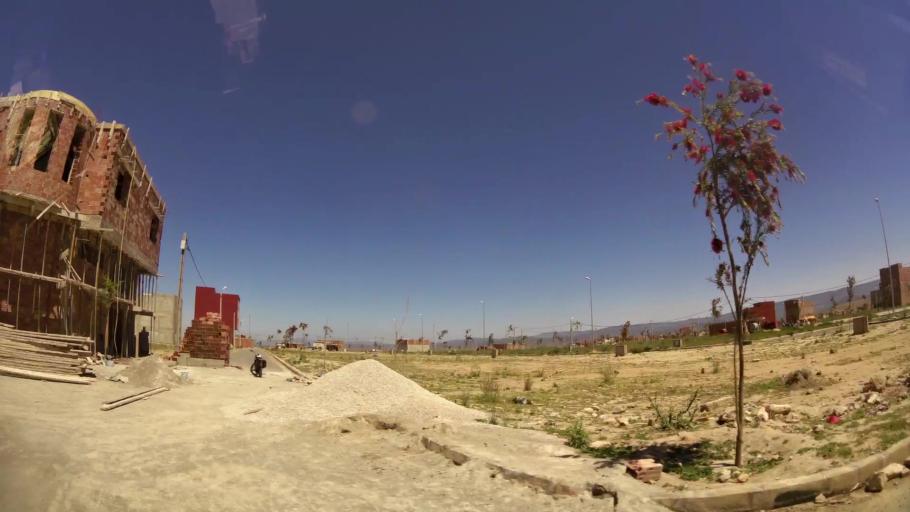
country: MA
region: Oriental
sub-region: Oujda-Angad
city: Oujda
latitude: 34.6848
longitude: -1.8647
